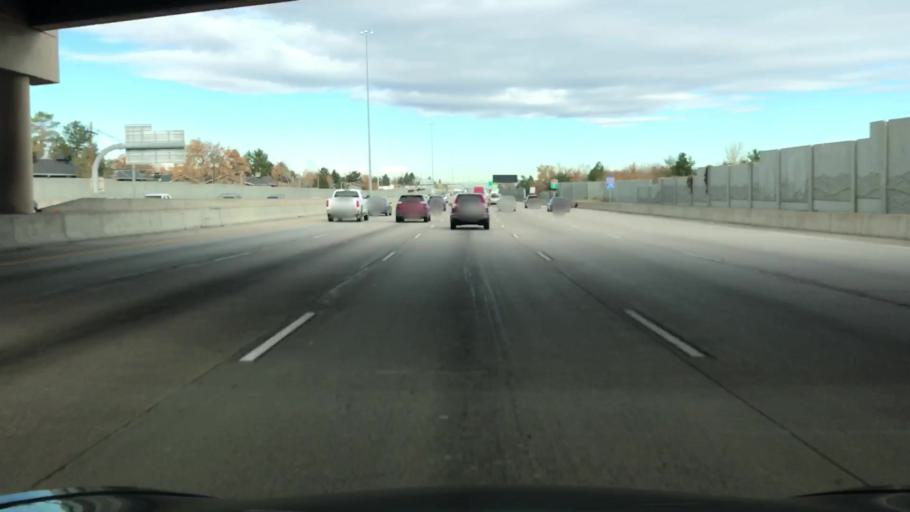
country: US
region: Colorado
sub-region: Arapahoe County
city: Greenwood Village
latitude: 39.6387
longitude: -104.9118
